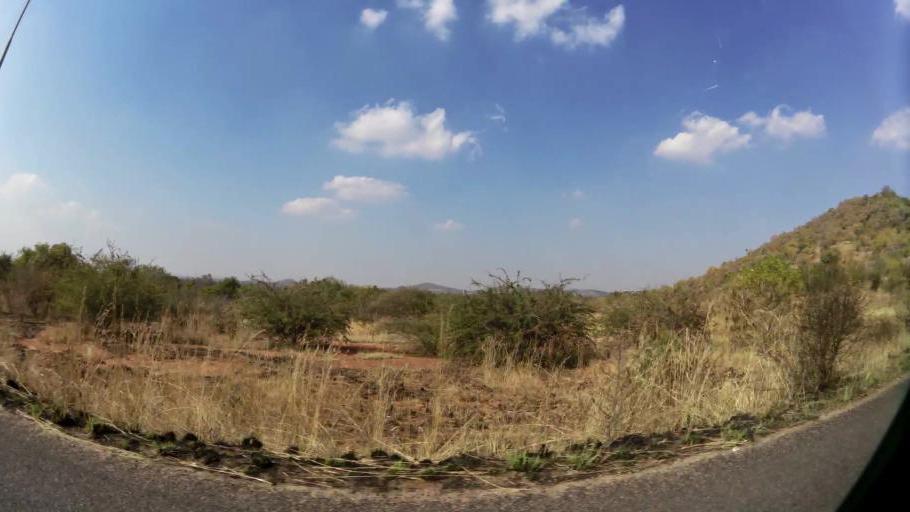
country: ZA
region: North-West
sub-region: Bojanala Platinum District Municipality
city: Rustenburg
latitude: -25.5690
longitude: 27.1408
